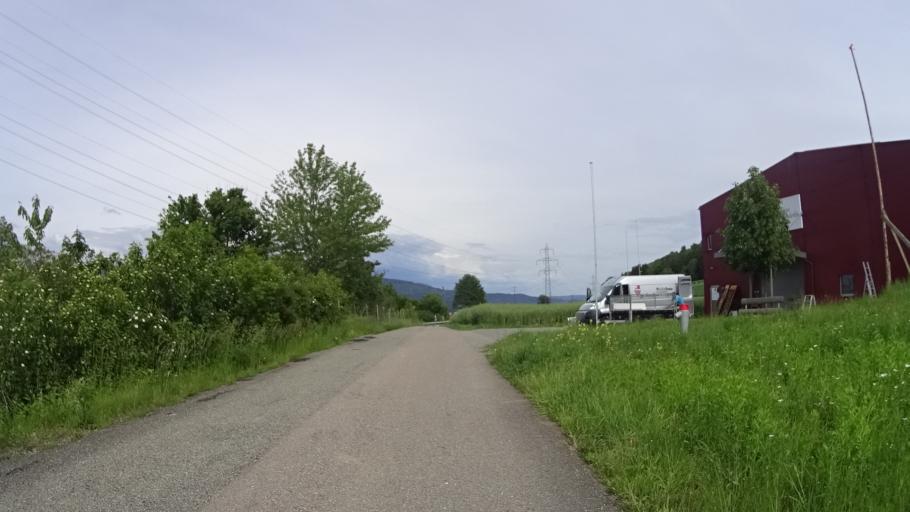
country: CH
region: Aargau
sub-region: Bezirk Rheinfelden
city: Mohlin
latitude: 47.5490
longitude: 7.8779
